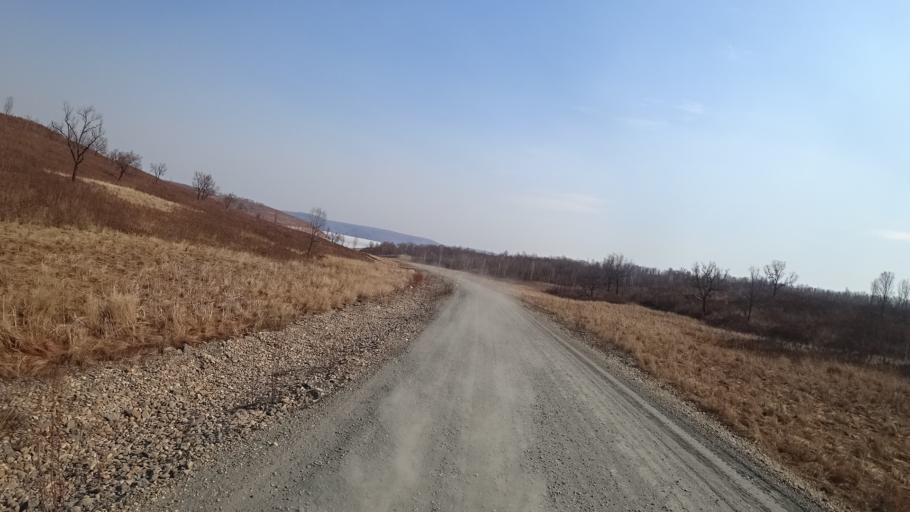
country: RU
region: Amur
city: Novobureyskiy
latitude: 49.8236
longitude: 129.9968
